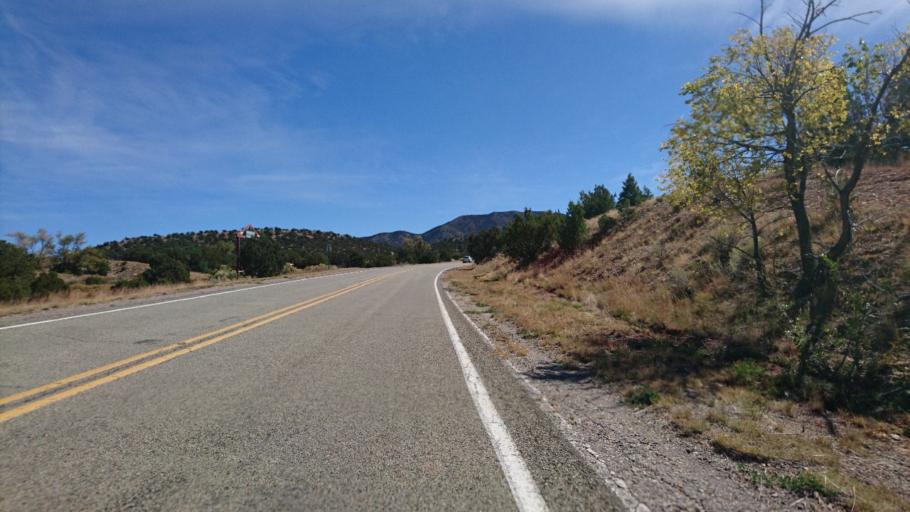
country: US
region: New Mexico
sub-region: Bernalillo County
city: Sandia Knolls
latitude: 35.2811
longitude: -106.2128
